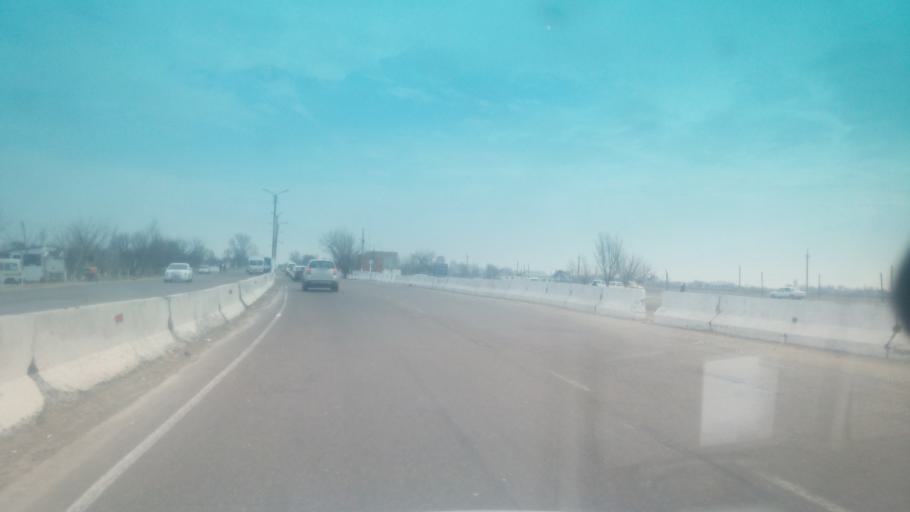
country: KZ
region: Ongtustik Qazaqstan
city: Myrzakent
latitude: 40.5038
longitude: 68.5212
